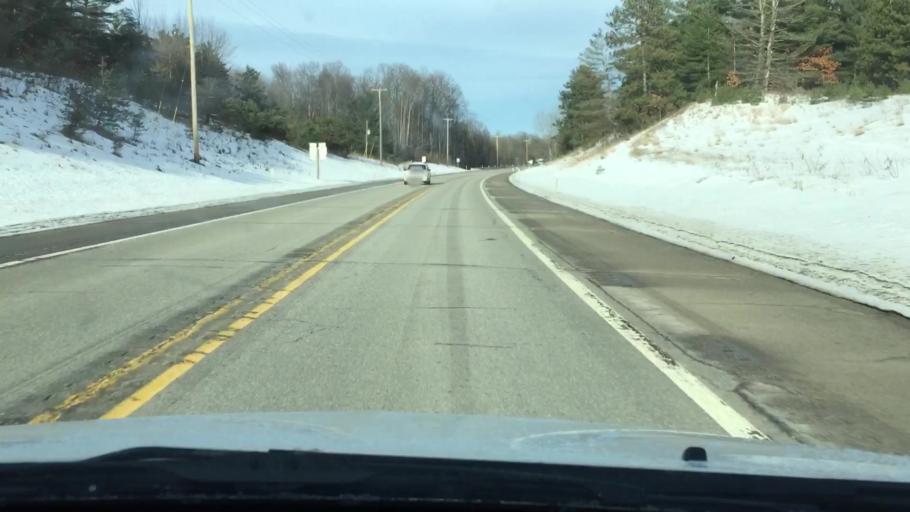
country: US
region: Michigan
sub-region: Wexford County
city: Manton
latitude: 44.5790
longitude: -85.3626
